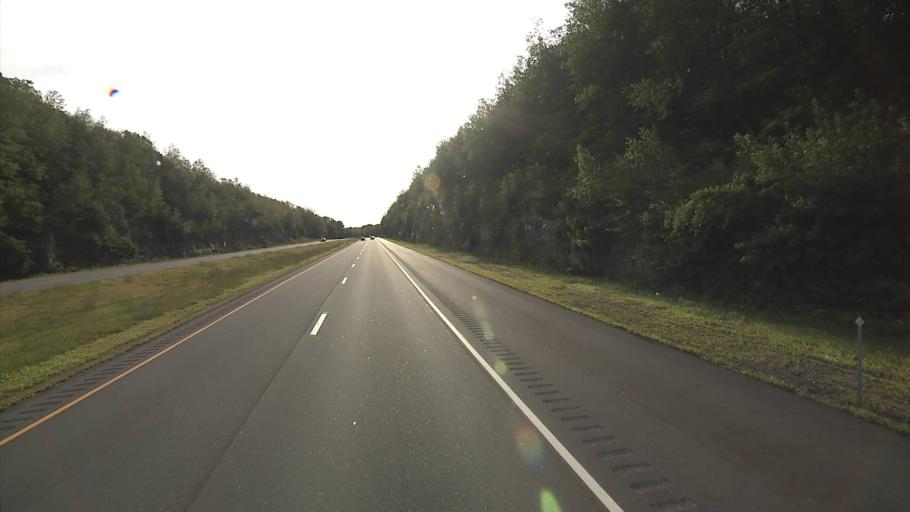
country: US
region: Connecticut
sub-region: New London County
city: Montville Center
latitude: 41.5711
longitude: -72.2002
